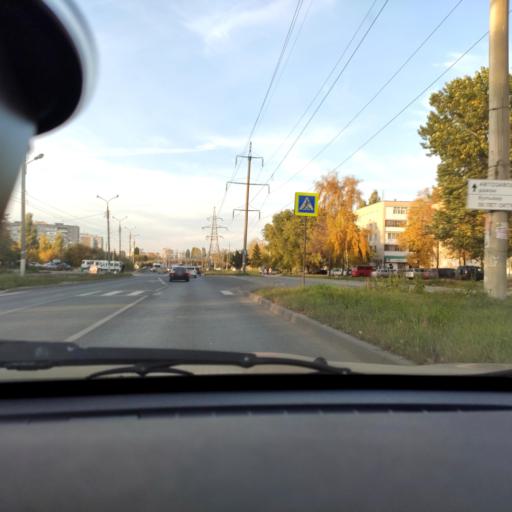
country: RU
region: Samara
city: Tol'yatti
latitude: 53.5271
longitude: 49.3964
